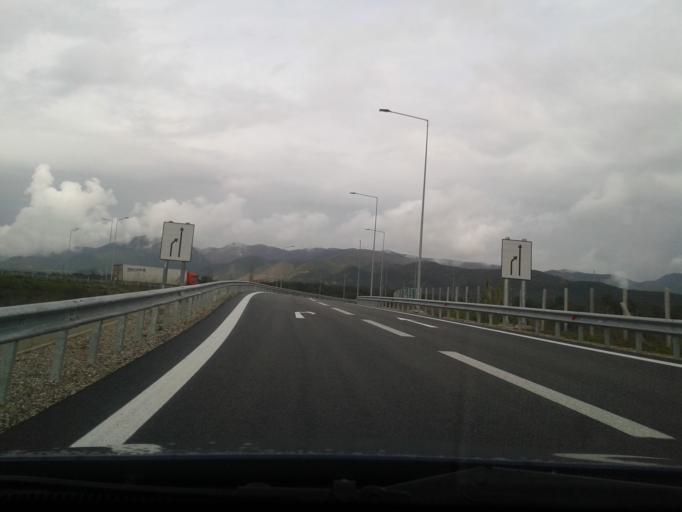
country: GR
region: West Greece
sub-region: Nomos Aitolias kai Akarnanias
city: Galatas
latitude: 38.3879
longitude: 21.5480
